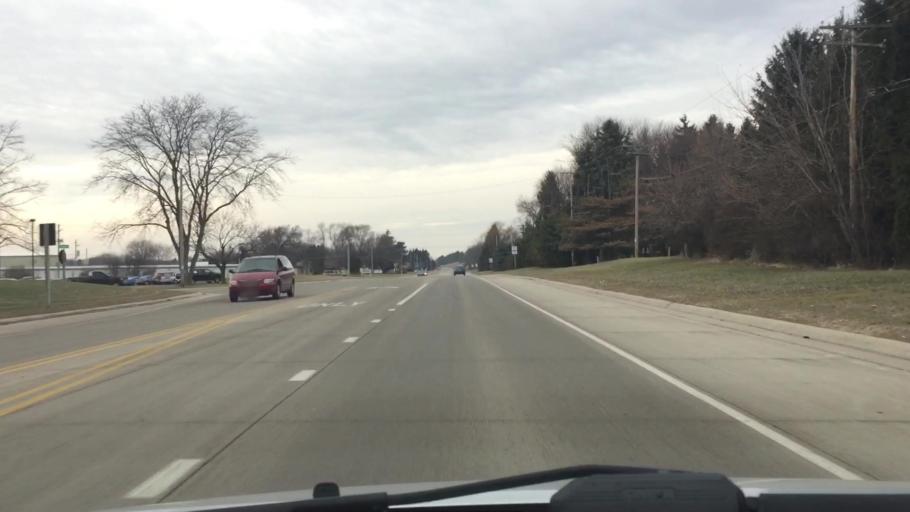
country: US
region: Wisconsin
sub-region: Waukesha County
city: Oconomowoc
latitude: 43.1248
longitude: -88.5304
